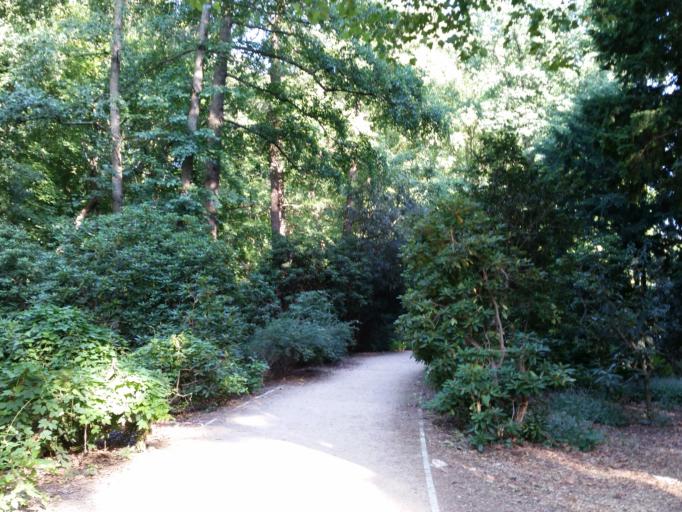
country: DE
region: Berlin
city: Hansaviertel
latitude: 52.5112
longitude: 13.3442
